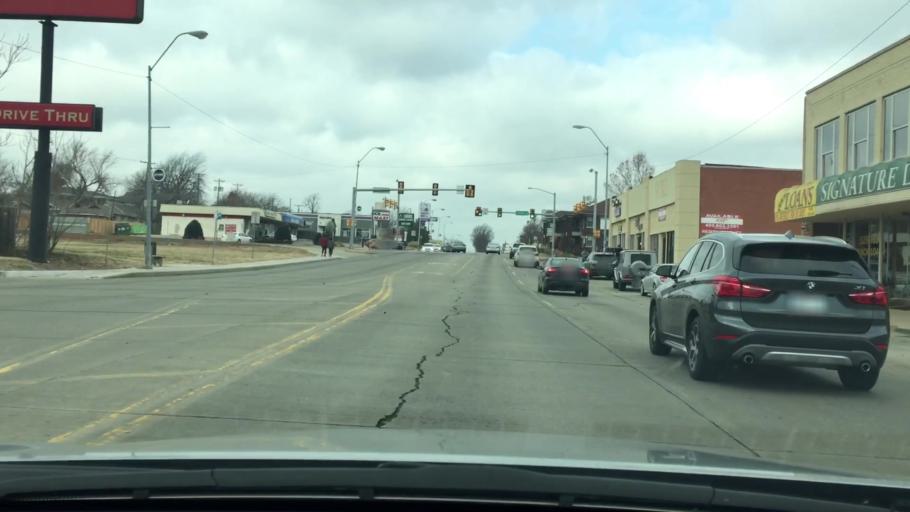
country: US
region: Oklahoma
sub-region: Oklahoma County
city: Oklahoma City
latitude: 35.4933
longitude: -97.5146
